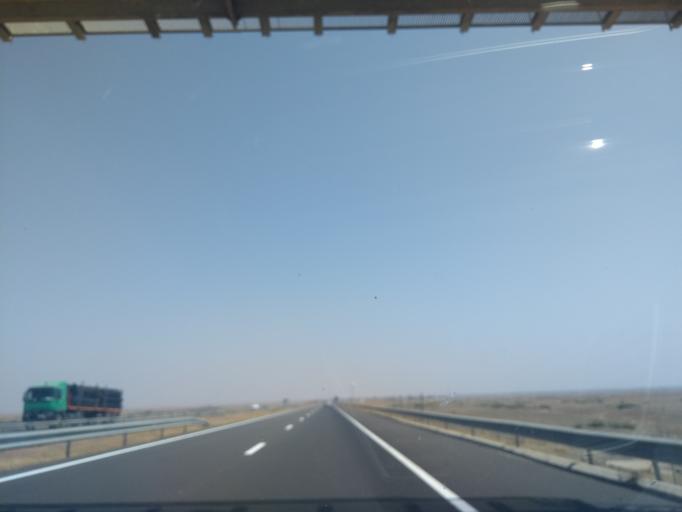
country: MA
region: Marrakech-Tensift-Al Haouz
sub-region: Kelaa-Des-Sraghna
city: Sidi Bou Othmane
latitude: 31.9019
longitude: -8.0252
